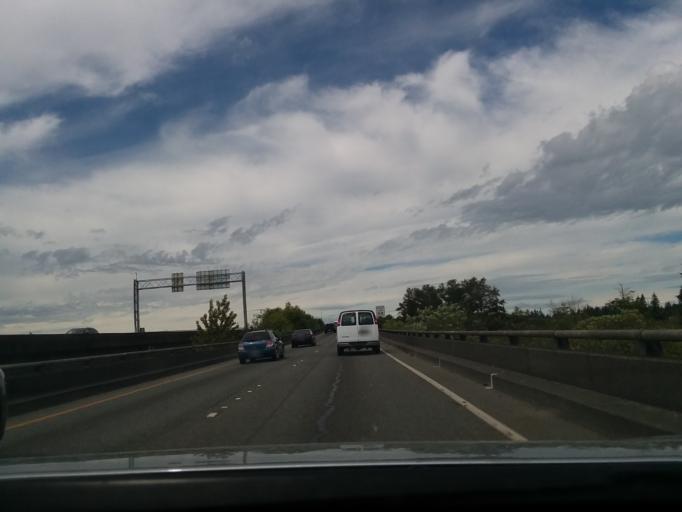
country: US
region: Washington
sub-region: Snohomish County
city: Everett
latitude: 47.9790
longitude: -122.1741
